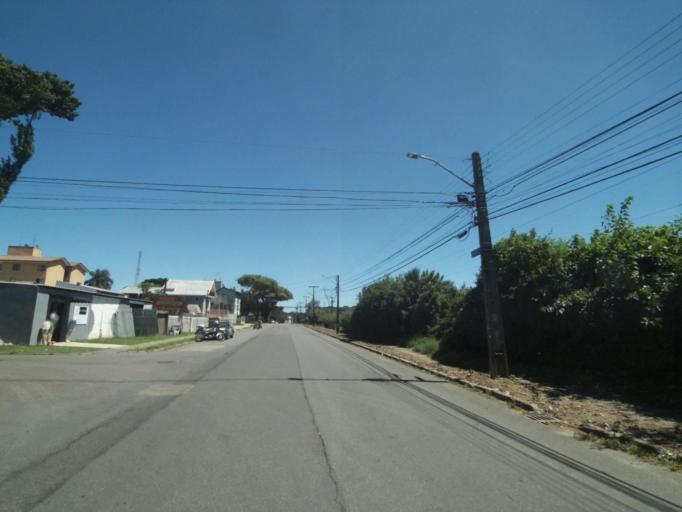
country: BR
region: Parana
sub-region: Curitiba
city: Curitiba
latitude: -25.4745
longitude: -49.3451
